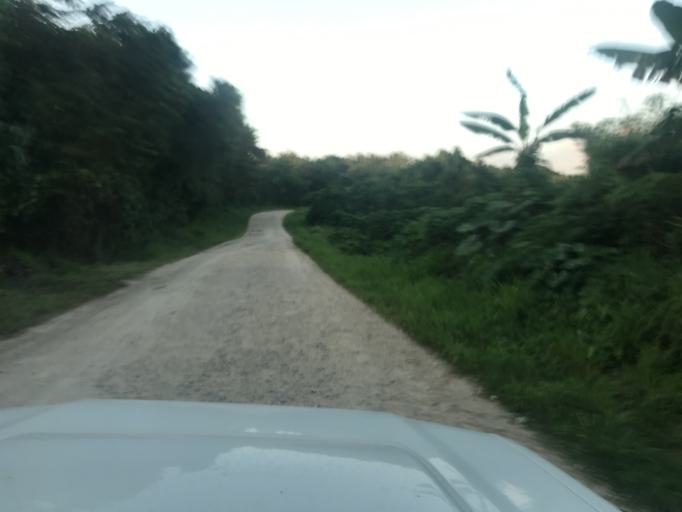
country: VU
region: Sanma
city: Luganville
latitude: -15.5630
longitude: 166.9597
